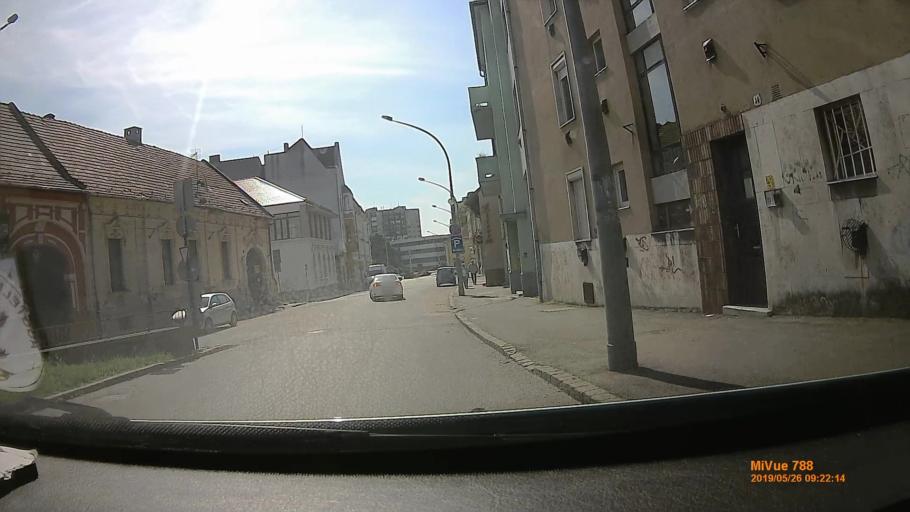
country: HU
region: Borsod-Abauj-Zemplen
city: Miskolc
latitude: 48.1001
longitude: 20.7829
